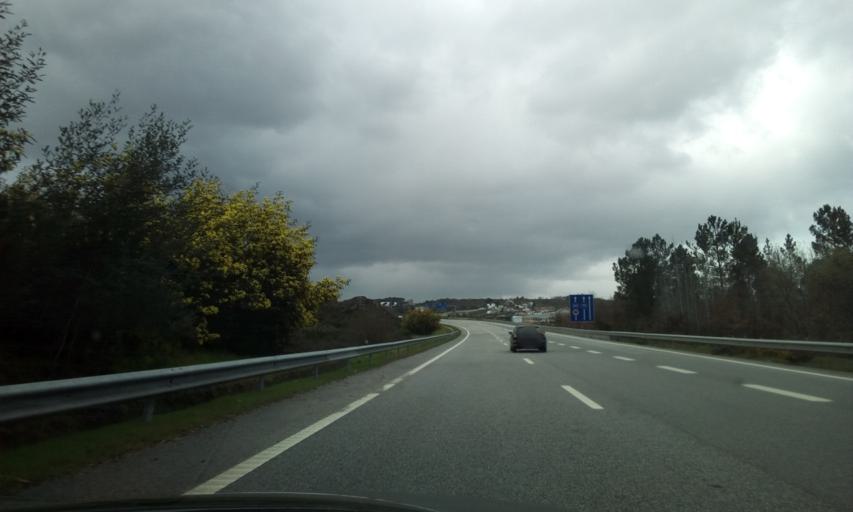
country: PT
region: Viseu
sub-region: Viseu
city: Rio de Loba
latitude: 40.6330
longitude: -7.8273
